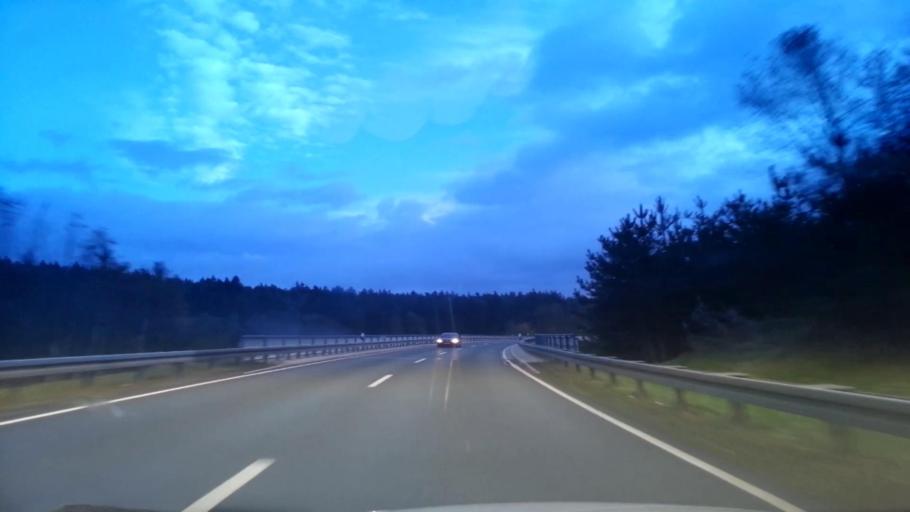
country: DE
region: Bavaria
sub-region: Upper Palatinate
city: Pechbrunn
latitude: 49.9711
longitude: 12.1775
